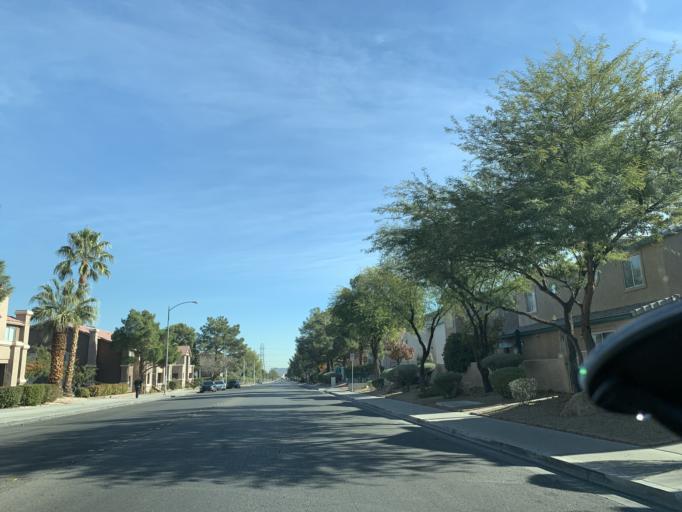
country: US
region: Nevada
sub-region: Clark County
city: Spring Valley
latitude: 36.0966
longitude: -115.2182
